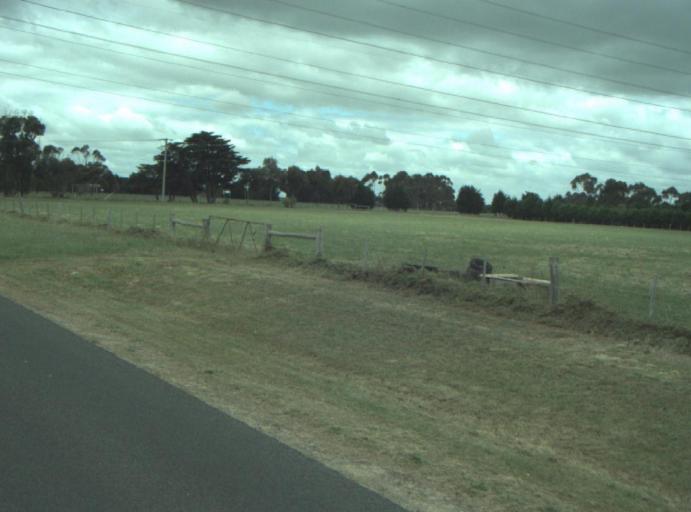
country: AU
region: Victoria
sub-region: Greater Geelong
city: Bell Post Hill
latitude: -38.0789
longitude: 144.3271
